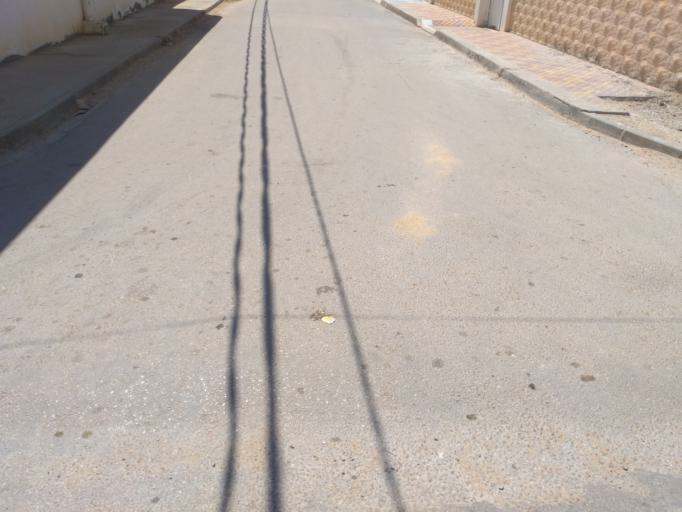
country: TN
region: Al Qayrawan
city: Kairouan
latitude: 35.6669
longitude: 10.0805
